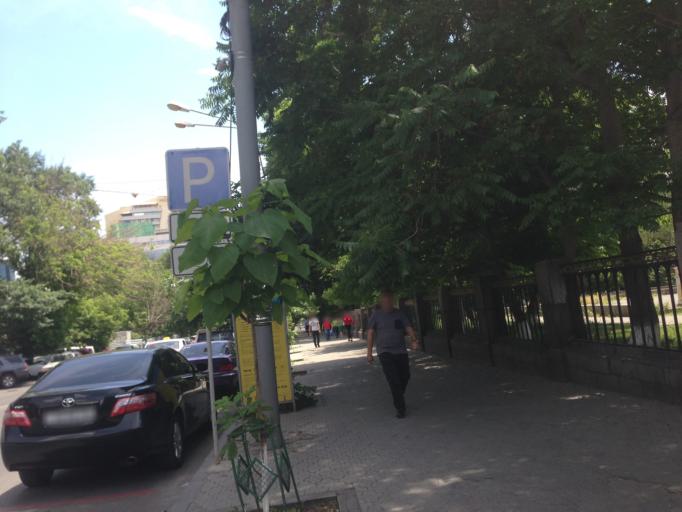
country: AM
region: Yerevan
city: Yerevan
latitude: 40.1773
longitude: 44.5077
